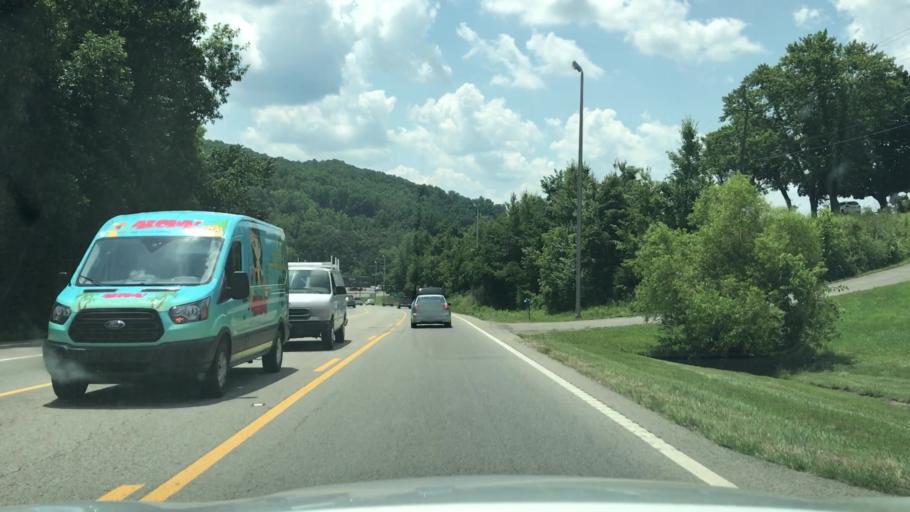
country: US
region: Tennessee
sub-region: Overton County
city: Livingston
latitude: 36.3815
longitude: -85.3349
